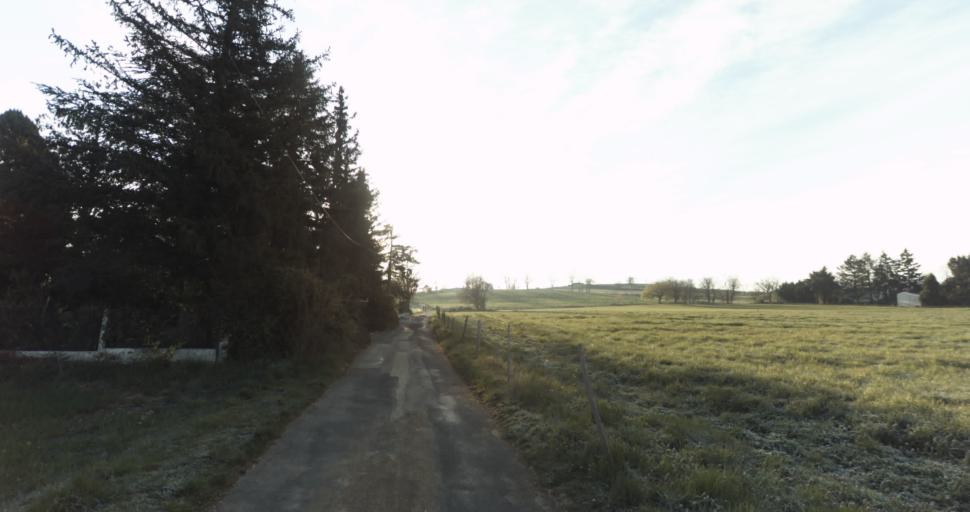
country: FR
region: Rhone-Alpes
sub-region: Departement de la Loire
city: Saint-Jean-Bonnefonds
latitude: 45.4541
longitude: 4.4316
